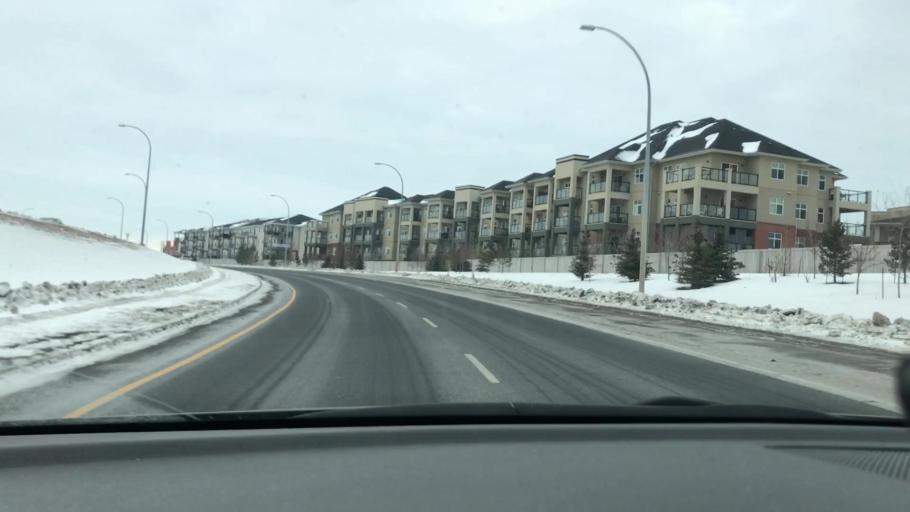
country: CA
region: Alberta
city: Edmonton
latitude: 53.5155
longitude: -113.4336
